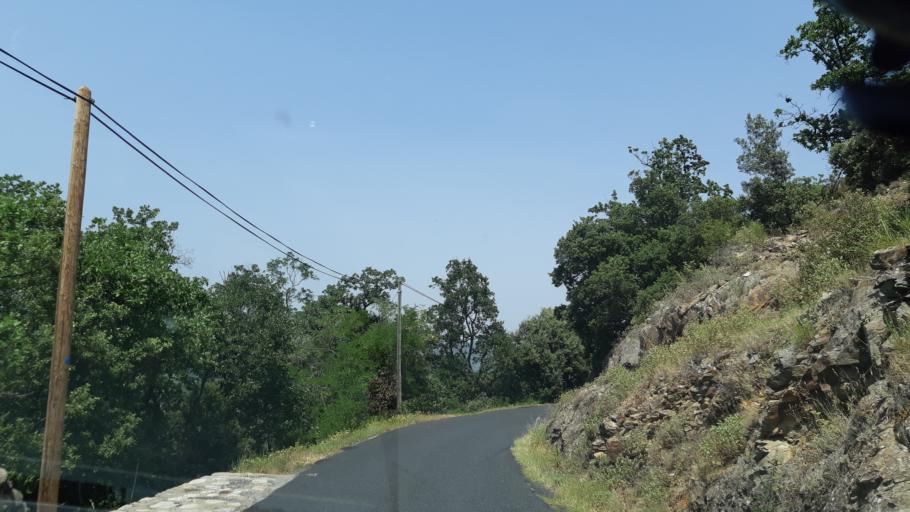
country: FR
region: Languedoc-Roussillon
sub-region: Departement des Pyrenees-Orientales
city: Vinca
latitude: 42.6106
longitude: 2.5127
